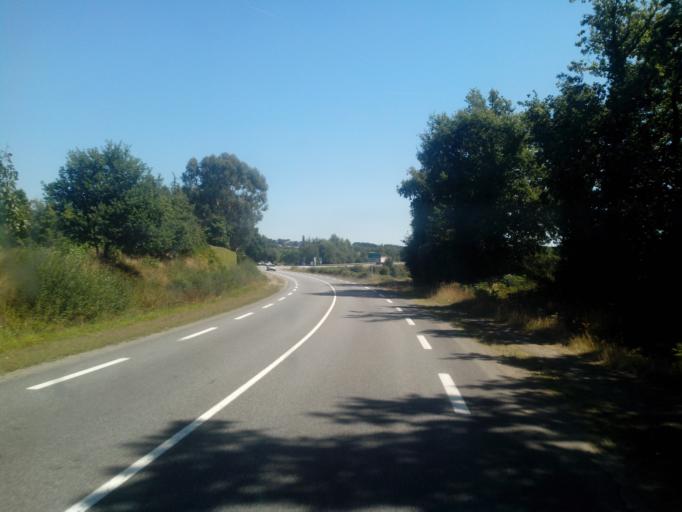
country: FR
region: Brittany
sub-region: Departement du Morbihan
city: Guegon
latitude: 47.9582
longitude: -2.5739
